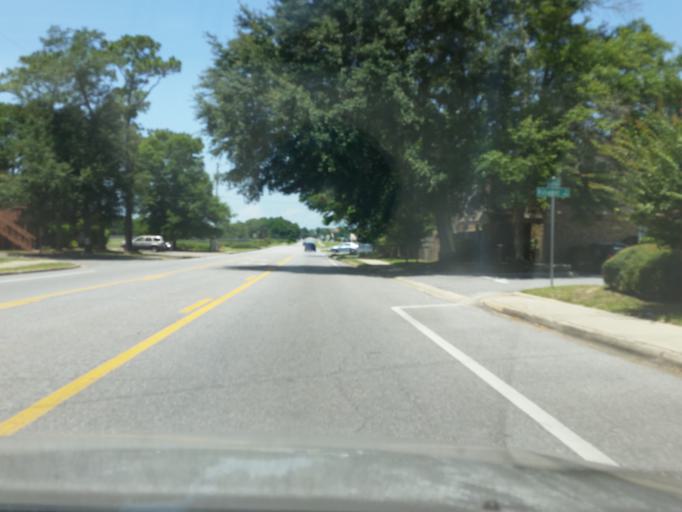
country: US
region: Florida
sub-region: Escambia County
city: Ferry Pass
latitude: 30.4878
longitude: -87.1885
